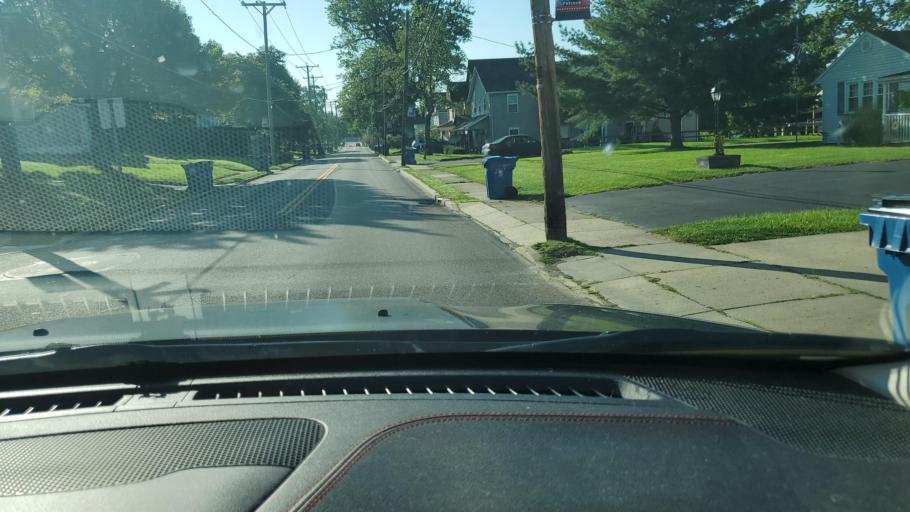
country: US
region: Ohio
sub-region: Mahoning County
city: Lowellville
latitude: 41.0394
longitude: -80.5383
